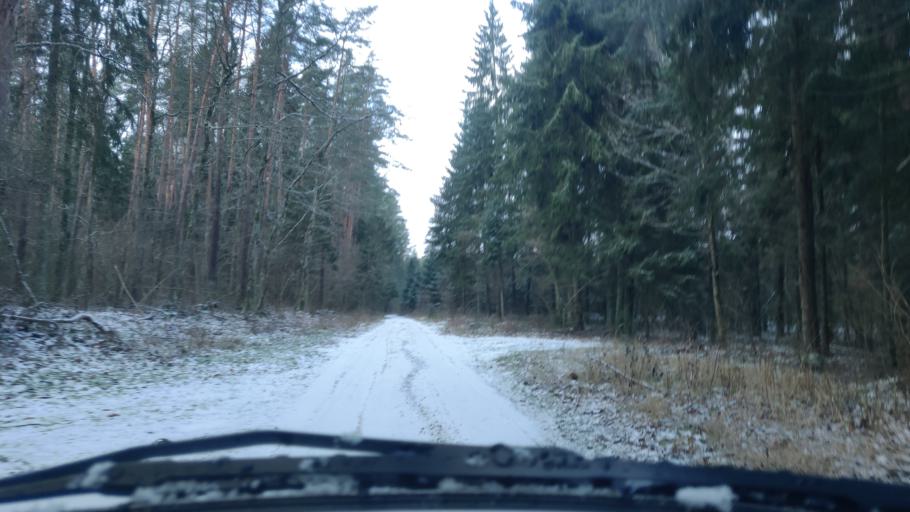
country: LT
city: Trakai
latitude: 54.5821
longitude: 24.9599
